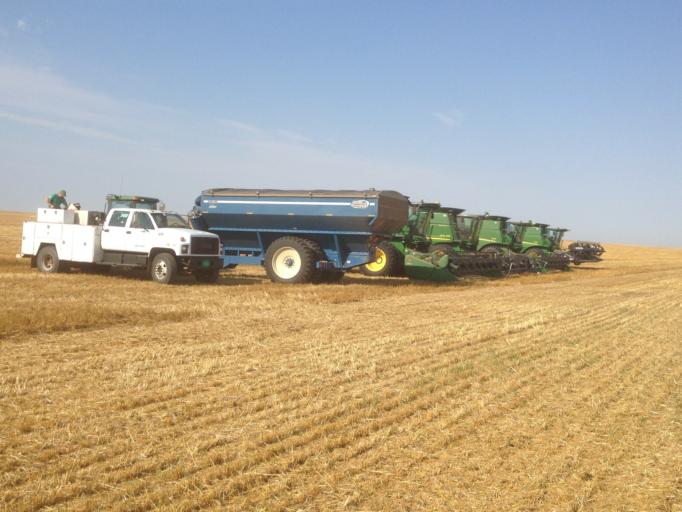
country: US
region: North Dakota
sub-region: Hettinger County
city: Mott
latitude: 46.4275
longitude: -102.6443
